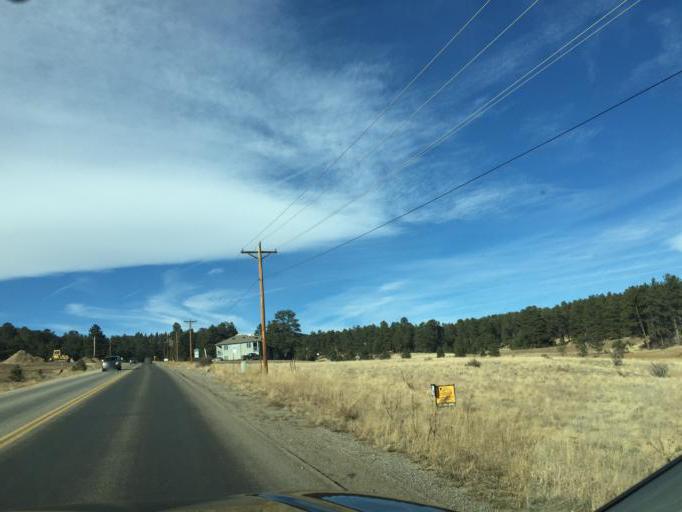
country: US
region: Colorado
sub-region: Jefferson County
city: Evergreen
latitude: 39.4408
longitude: -105.4546
